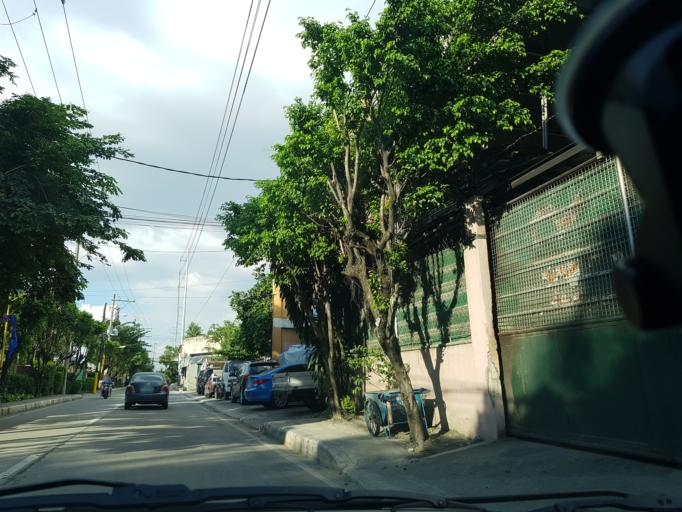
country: PH
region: Metro Manila
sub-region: Marikina
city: Calumpang
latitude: 14.6188
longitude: 121.0819
